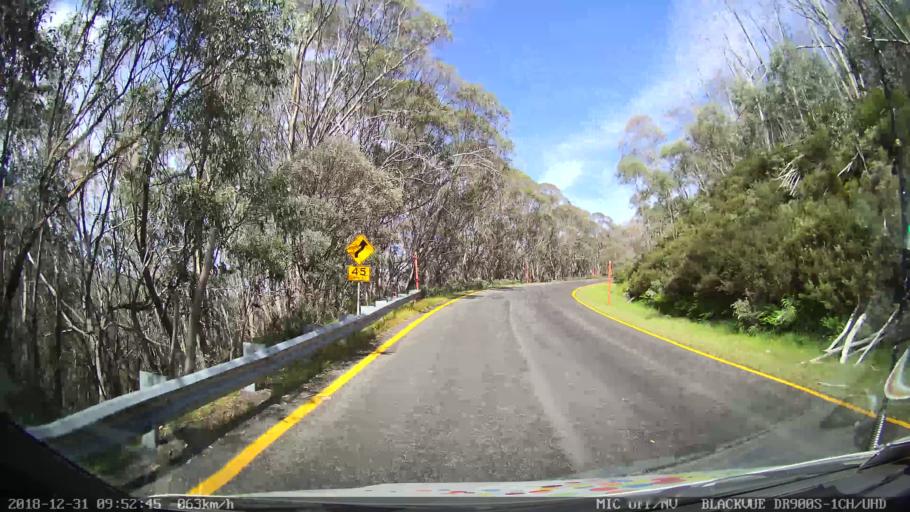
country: AU
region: New South Wales
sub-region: Snowy River
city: Jindabyne
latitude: -36.5287
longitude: 148.2497
